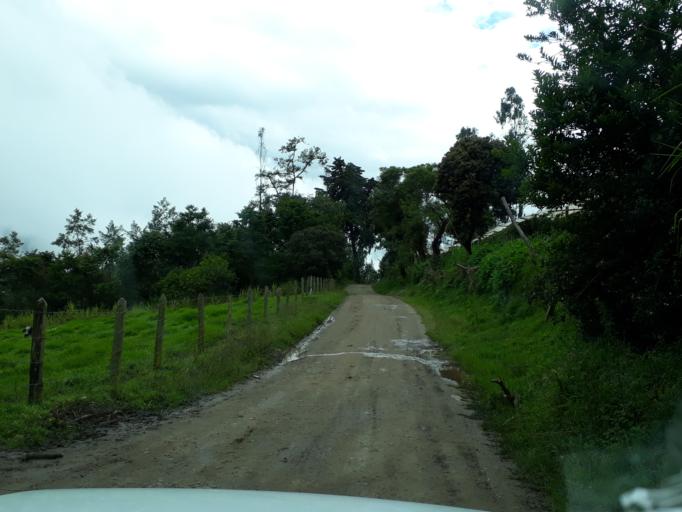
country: CO
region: Cundinamarca
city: Junin
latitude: 4.7975
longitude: -73.6600
